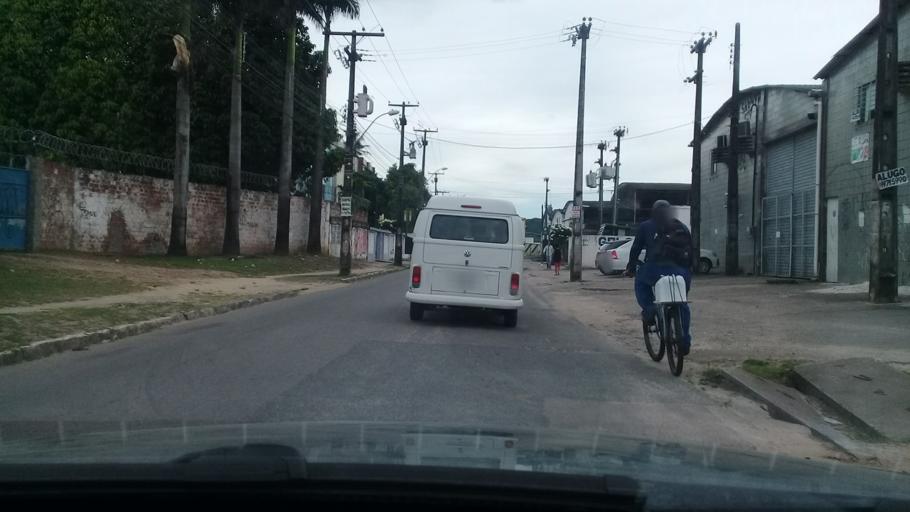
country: BR
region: Pernambuco
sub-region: Sao Lourenco Da Mata
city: Sao Lourenco da Mata
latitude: -8.0321
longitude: -34.9592
